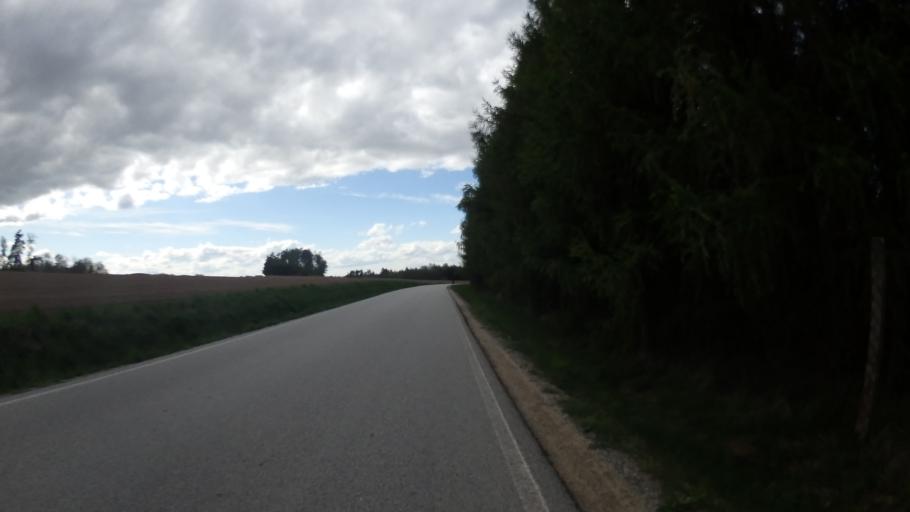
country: CZ
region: Vysocina
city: Merin
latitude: 49.3688
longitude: 15.8983
